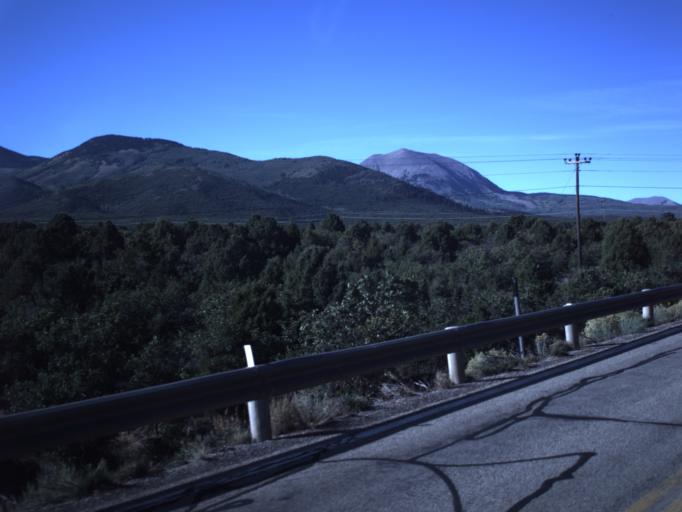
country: US
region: Utah
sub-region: Grand County
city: Moab
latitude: 38.3410
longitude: -109.2092
